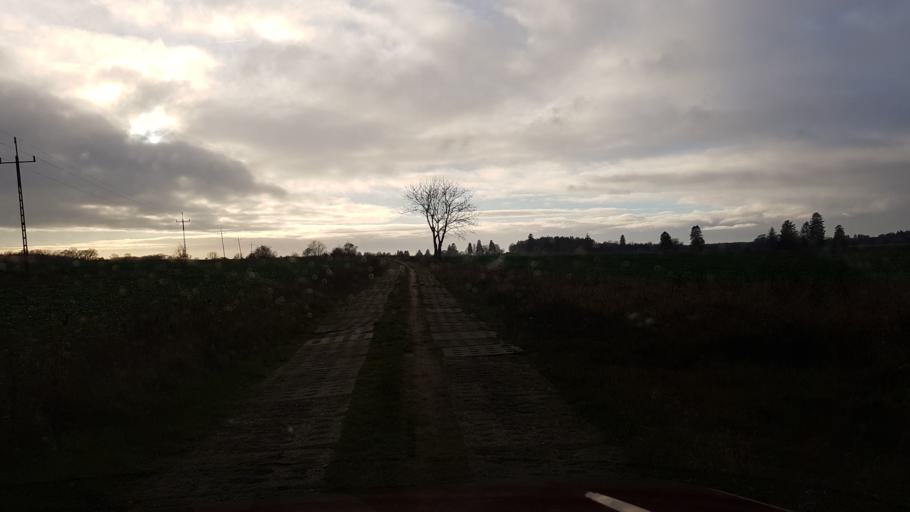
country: PL
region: West Pomeranian Voivodeship
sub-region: Powiat szczecinecki
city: Grzmiaca
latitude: 53.9920
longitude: 16.4130
